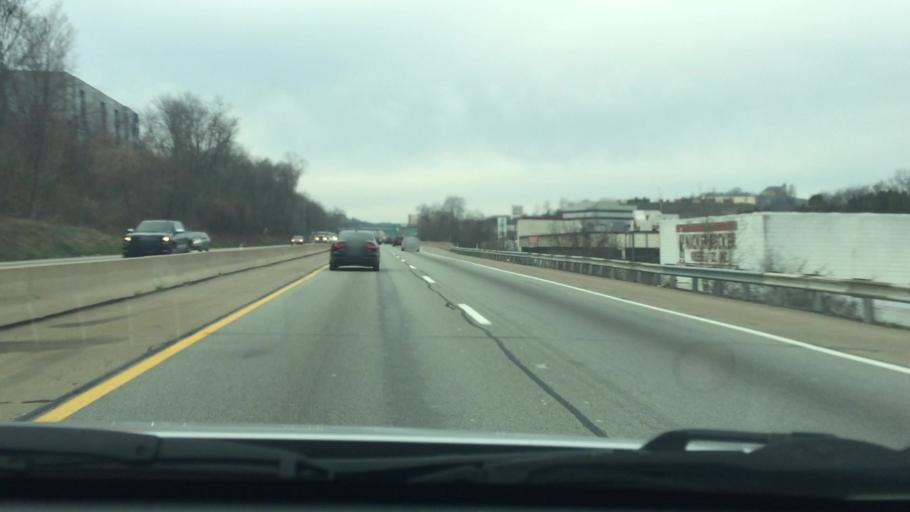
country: US
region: Pennsylvania
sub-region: Allegheny County
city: Rennerdale
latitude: 40.4327
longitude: -80.1405
